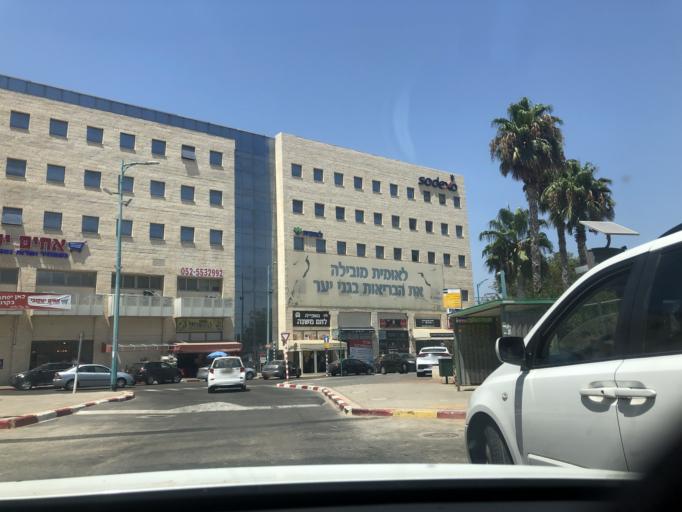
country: IL
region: Central District
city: Lod
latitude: 31.9445
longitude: 34.9014
